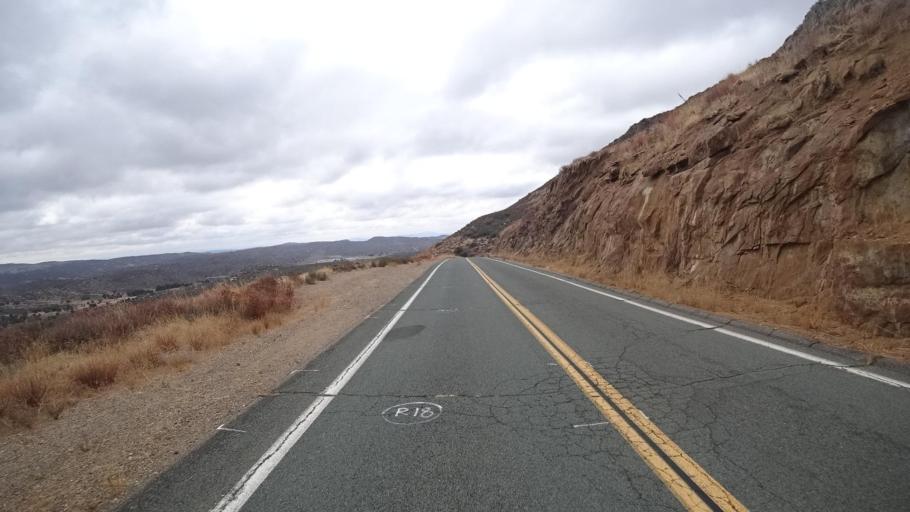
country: US
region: California
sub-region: San Diego County
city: Pine Valley
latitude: 32.7434
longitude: -116.4529
